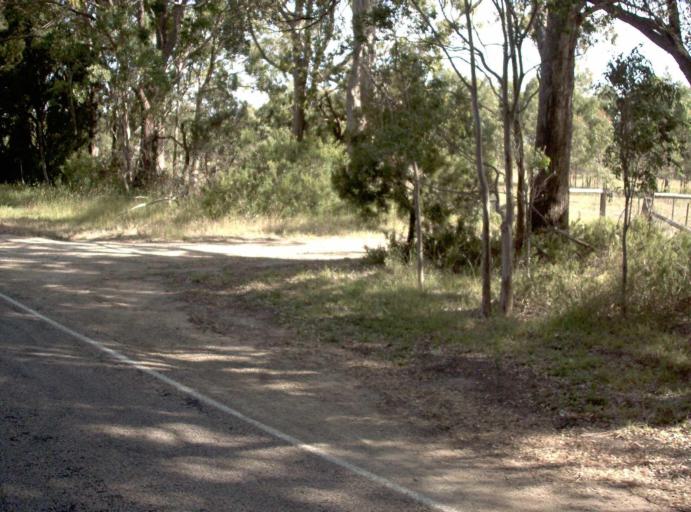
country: AU
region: Victoria
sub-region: East Gippsland
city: Lakes Entrance
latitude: -37.8000
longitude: 147.8346
